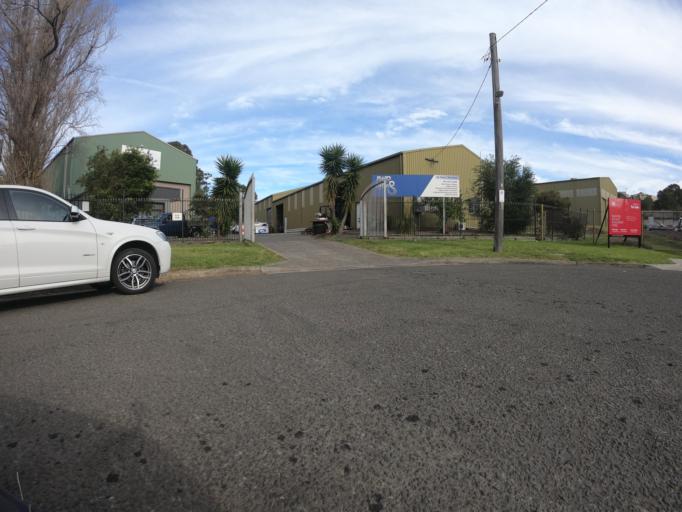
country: AU
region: New South Wales
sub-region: Wollongong
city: Port Kembla
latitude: -34.4795
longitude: 150.8908
